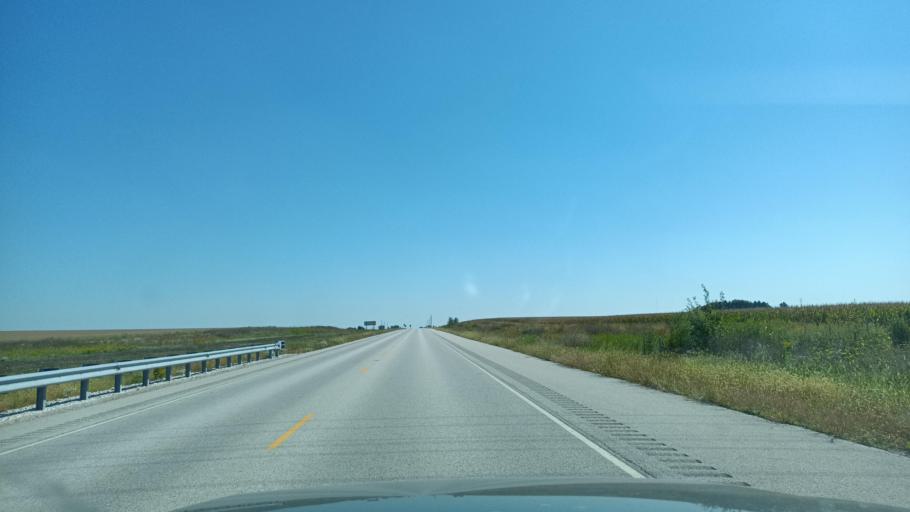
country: US
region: Illinois
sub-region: McDonough County
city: Macomb
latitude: 40.5033
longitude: -90.6944
